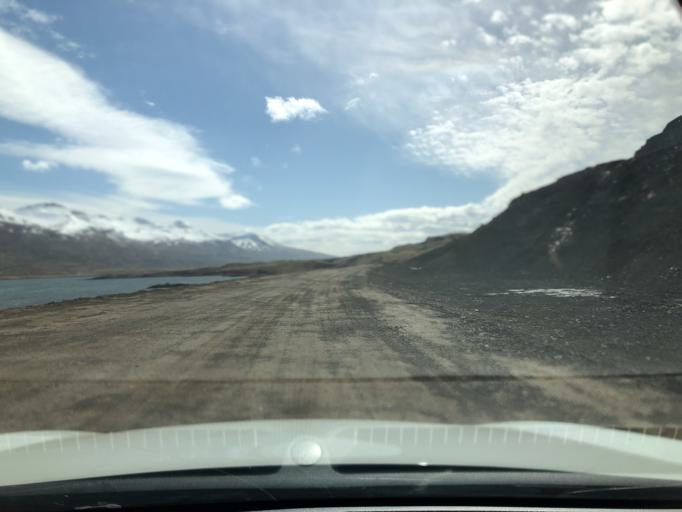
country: IS
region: East
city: Reydarfjoerdur
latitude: 64.7837
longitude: -14.4852
